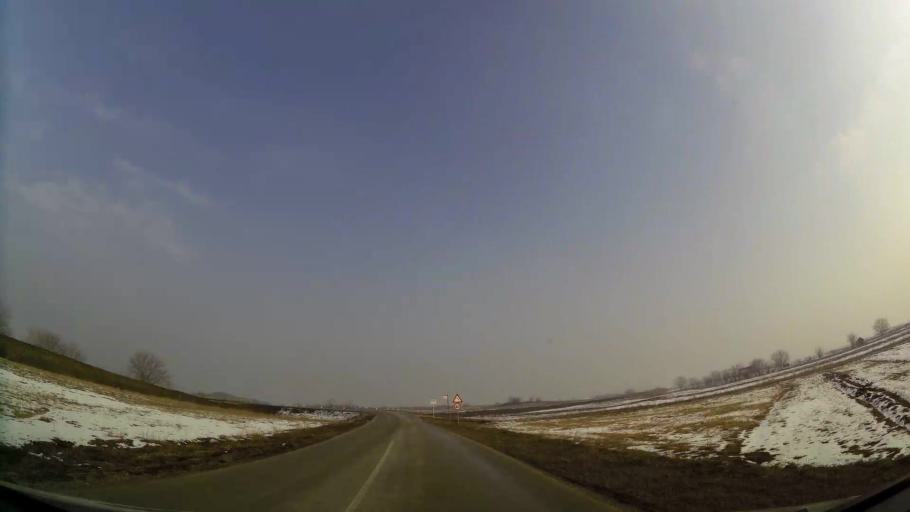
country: MK
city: Kadino
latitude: 41.9728
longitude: 21.6059
